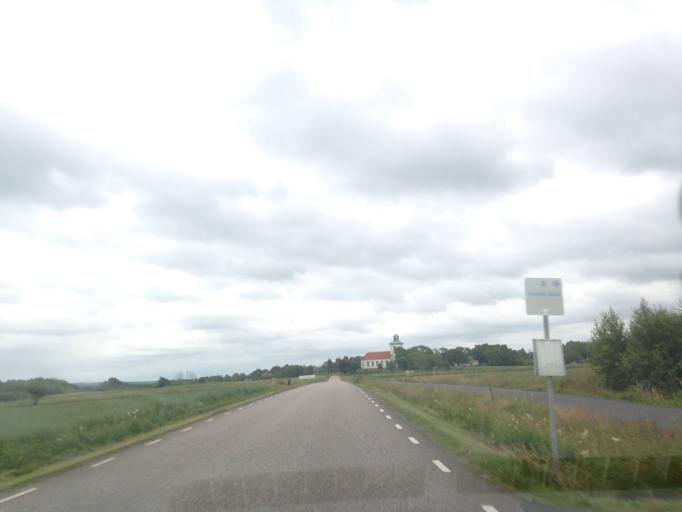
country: SE
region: Vaestra Goetaland
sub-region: Goteborg
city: Torslanda
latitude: 57.8196
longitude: 11.8310
